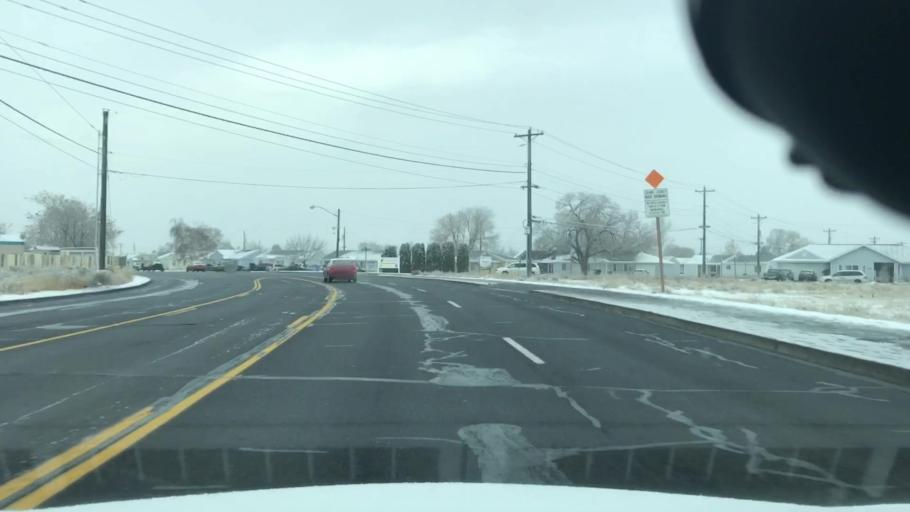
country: US
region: Washington
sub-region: Grant County
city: Moses Lake North
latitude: 47.1791
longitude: -119.3227
